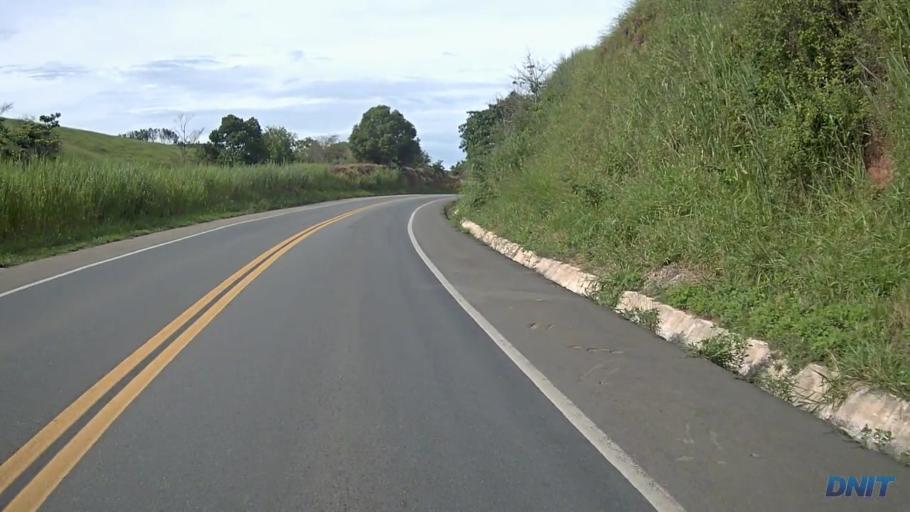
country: BR
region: Minas Gerais
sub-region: Belo Oriente
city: Belo Oriente
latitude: -19.2123
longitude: -42.3063
